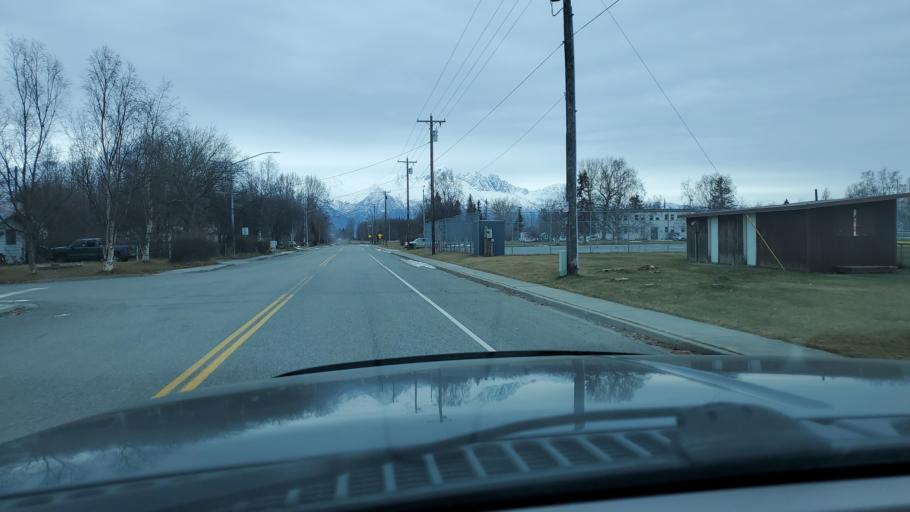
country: US
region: Alaska
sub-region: Matanuska-Susitna Borough
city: Palmer
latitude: 61.5997
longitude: -149.1031
